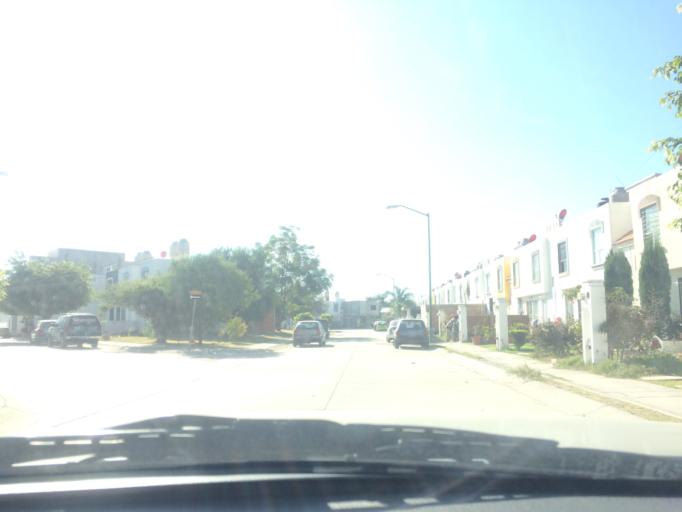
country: MX
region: Guanajuato
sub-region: Leon
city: Fraccionamiento Paraiso Real
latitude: 21.1058
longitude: -101.5980
